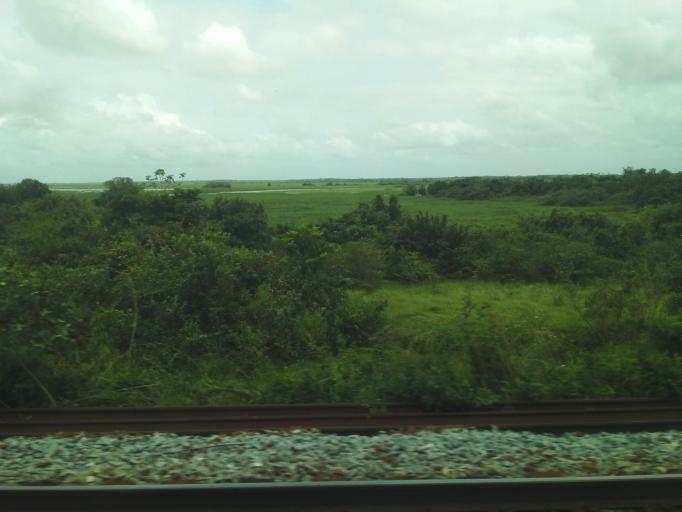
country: BR
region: Maranhao
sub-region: Arari
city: Arari
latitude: -3.5771
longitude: -44.7572
